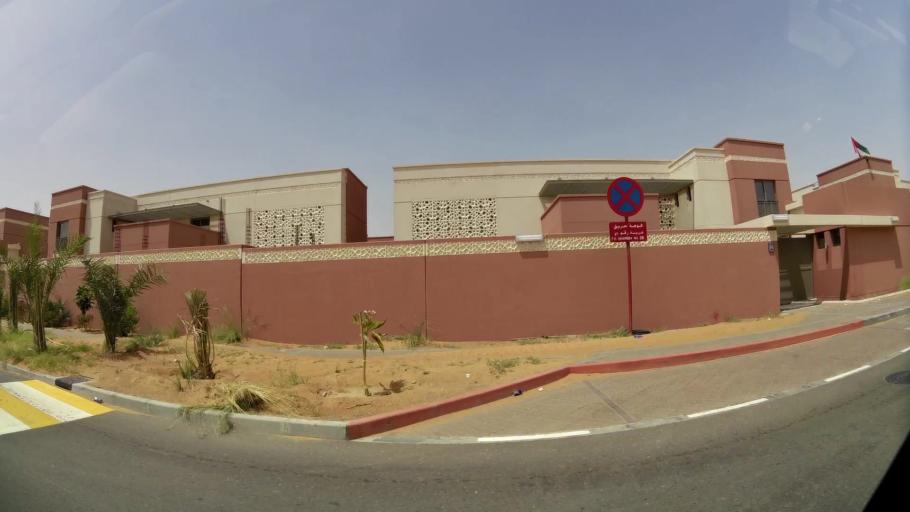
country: AE
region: Abu Dhabi
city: Al Ain
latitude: 24.1426
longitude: 55.6172
